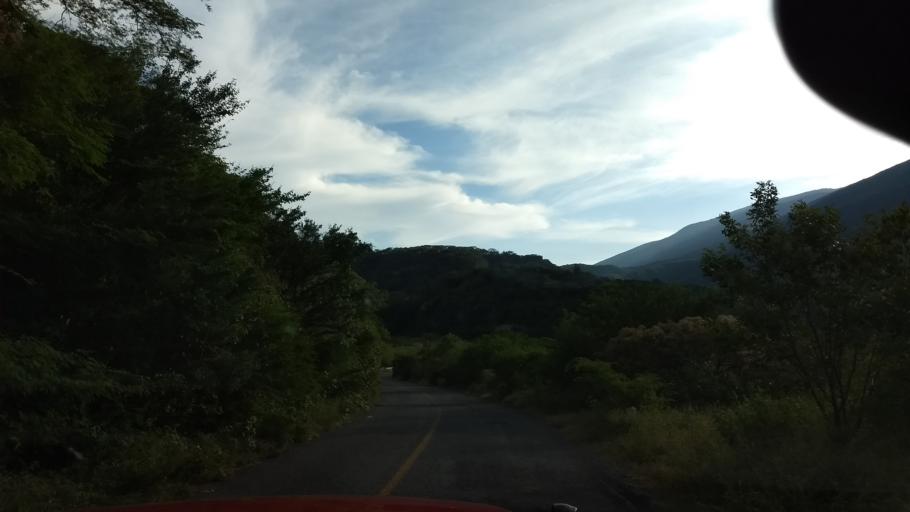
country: MX
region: Colima
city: Suchitlan
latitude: 19.4575
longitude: -103.8229
